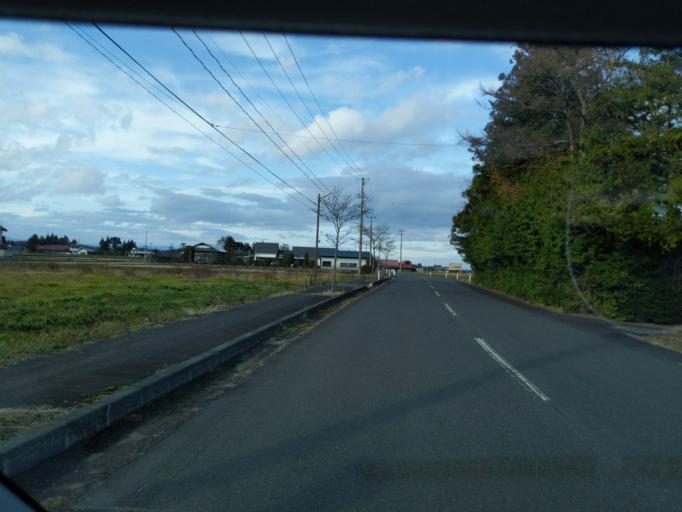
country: JP
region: Iwate
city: Mizusawa
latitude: 39.1435
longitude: 141.0892
